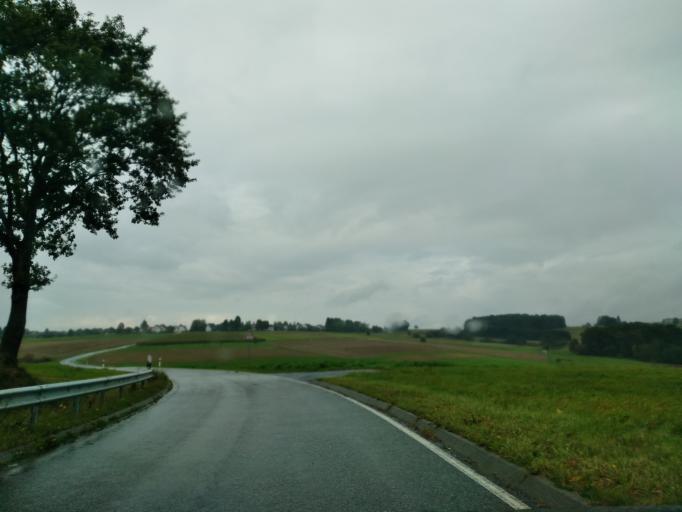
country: DE
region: Rheinland-Pfalz
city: Hirz-Maulsbach
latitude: 50.6777
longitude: 7.4525
